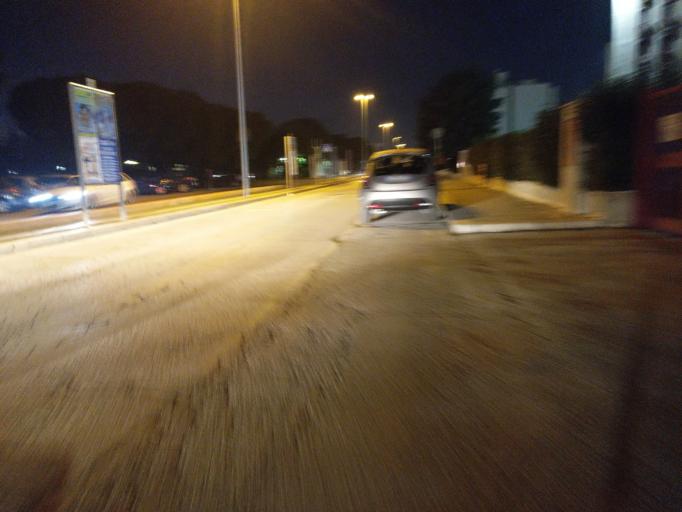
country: IT
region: Apulia
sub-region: Provincia di Bari
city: Modugno
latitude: 41.0795
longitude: 16.7886
